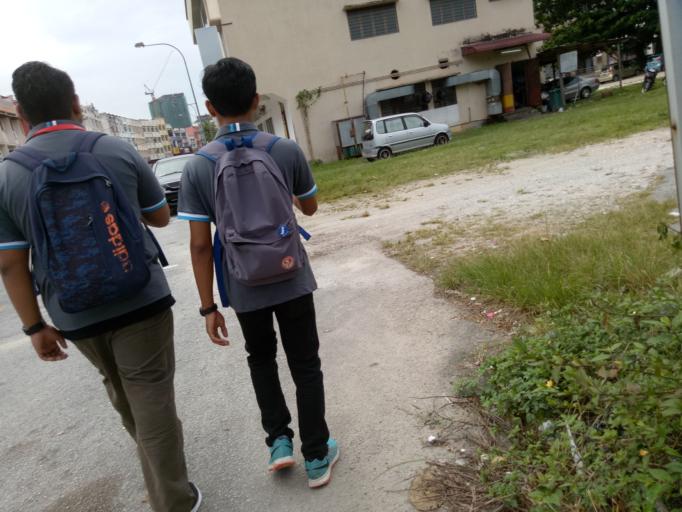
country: MY
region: Perak
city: Ipoh
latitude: 4.6008
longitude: 101.0829
